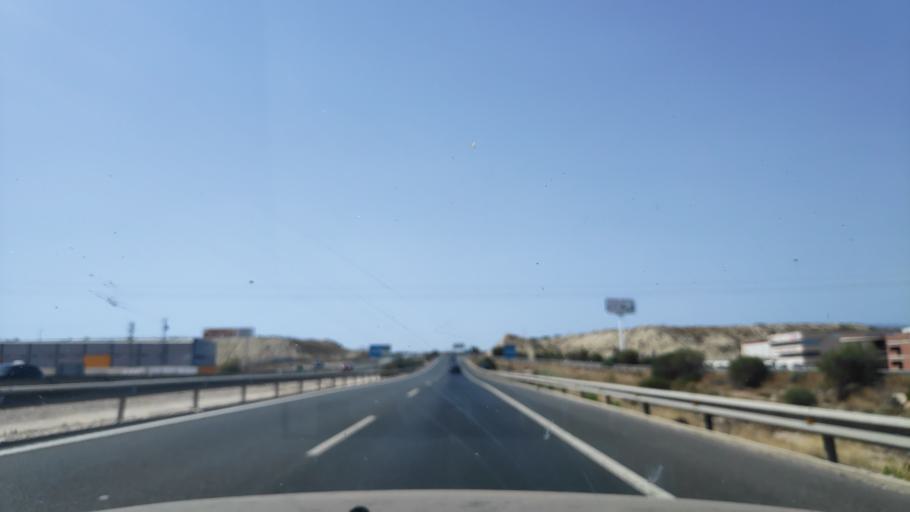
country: ES
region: Murcia
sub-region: Murcia
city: Lorqui
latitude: 38.1025
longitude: -1.2338
